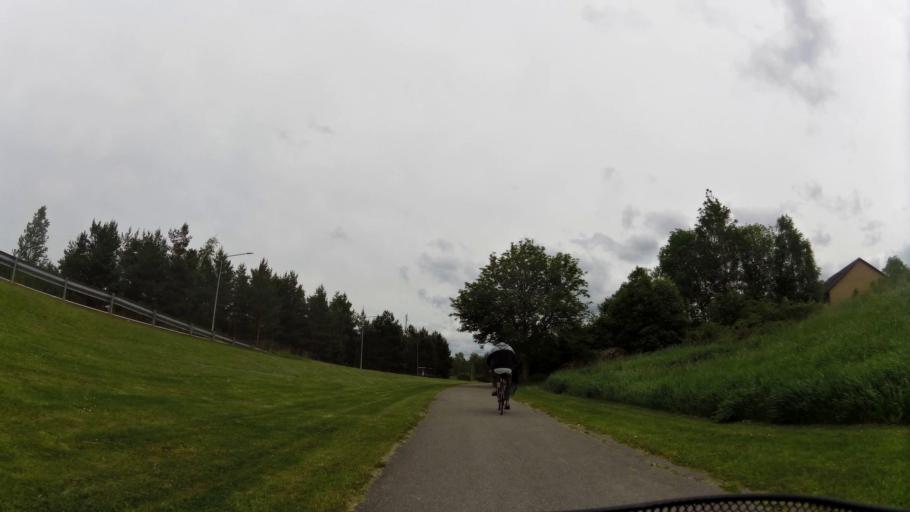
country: SE
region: OEstergoetland
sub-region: Linkopings Kommun
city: Malmslatt
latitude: 58.3897
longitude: 15.5678
